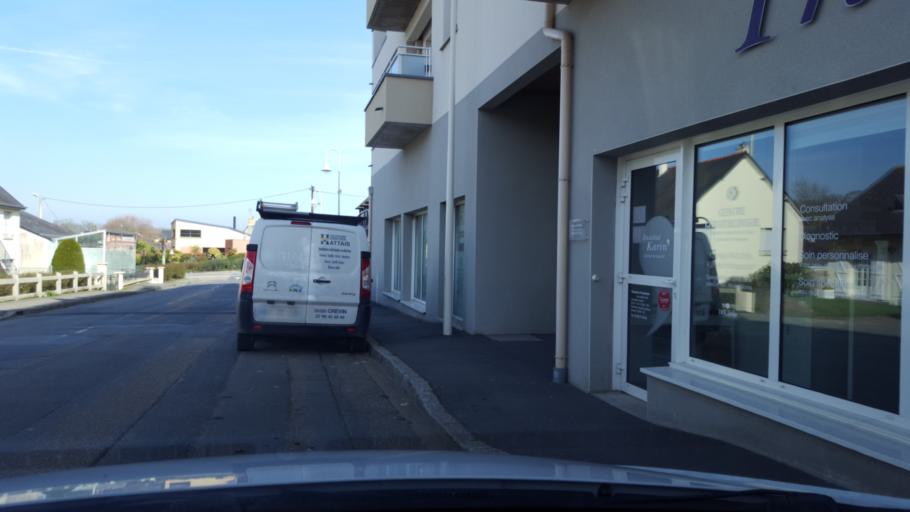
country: FR
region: Brittany
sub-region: Departement d'Ille-et-Vilaine
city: Guichen
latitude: 47.9679
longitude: -1.7982
